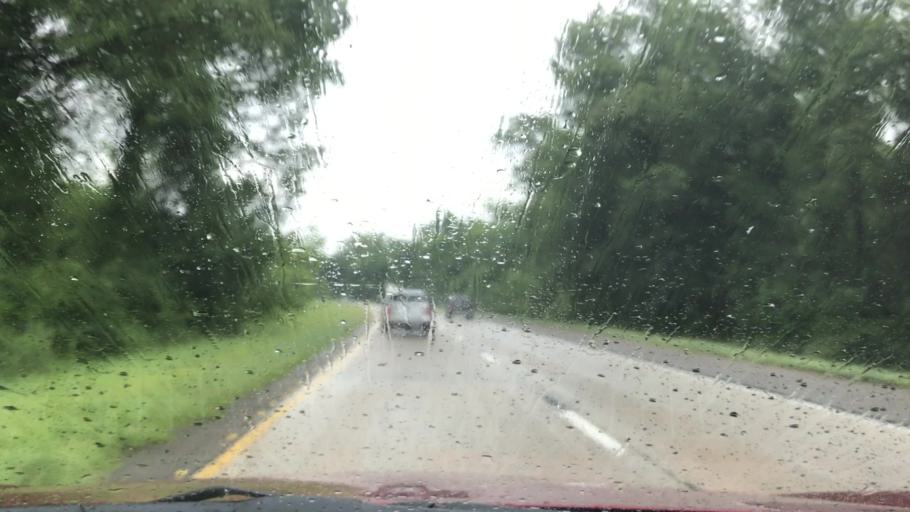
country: US
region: South Carolina
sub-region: Orangeburg County
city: Holly Hill
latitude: 33.2364
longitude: -80.4562
